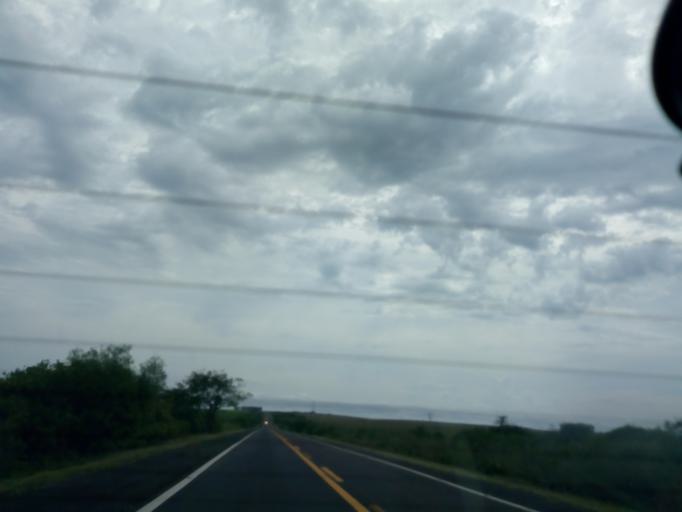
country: BR
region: Rio Grande do Sul
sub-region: Alegrete
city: Alegrete
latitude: -29.8635
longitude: -55.9544
